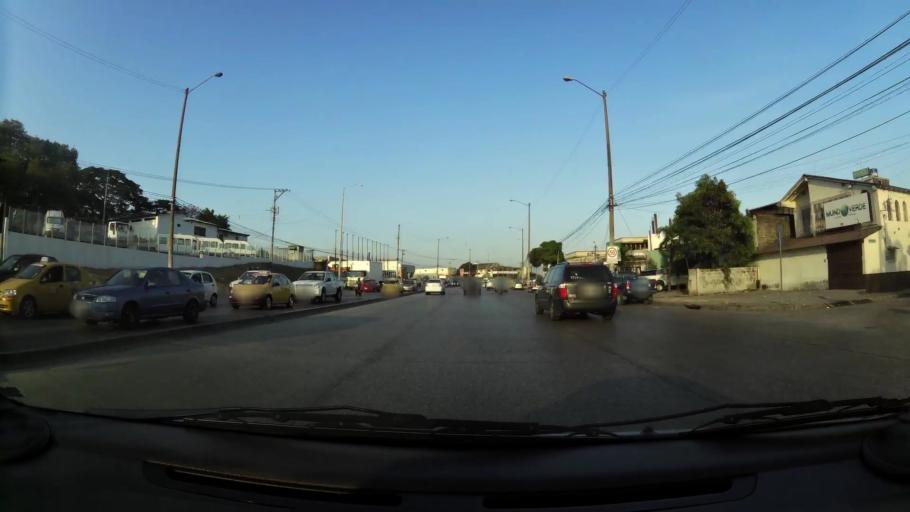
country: EC
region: Guayas
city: Guayaquil
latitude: -2.1403
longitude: -79.9276
